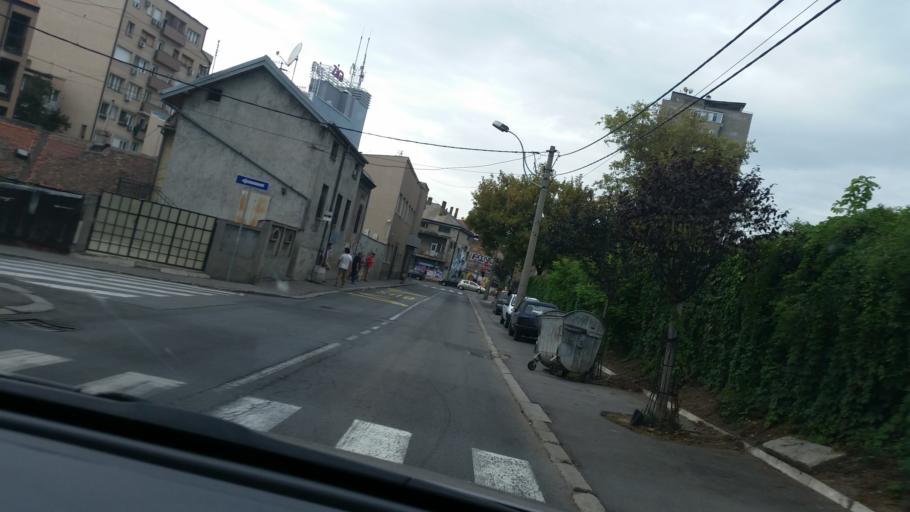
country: RS
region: Central Serbia
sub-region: Belgrade
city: Vracar
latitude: 44.8083
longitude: 20.4844
